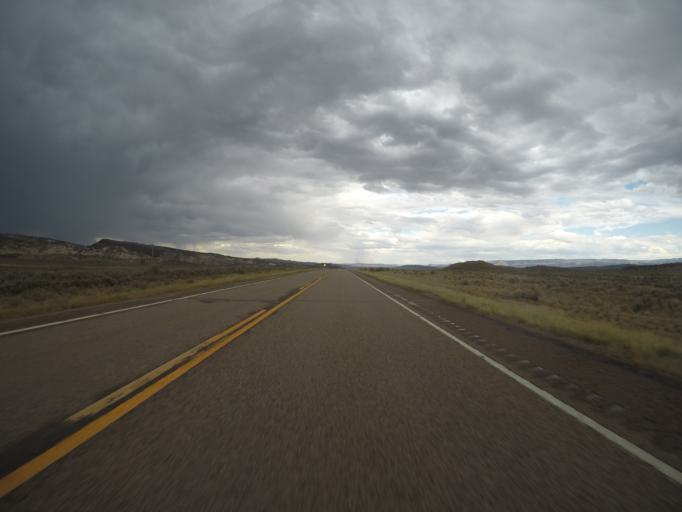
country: US
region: Colorado
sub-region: Rio Blanco County
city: Rangely
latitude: 40.2513
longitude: -108.7997
